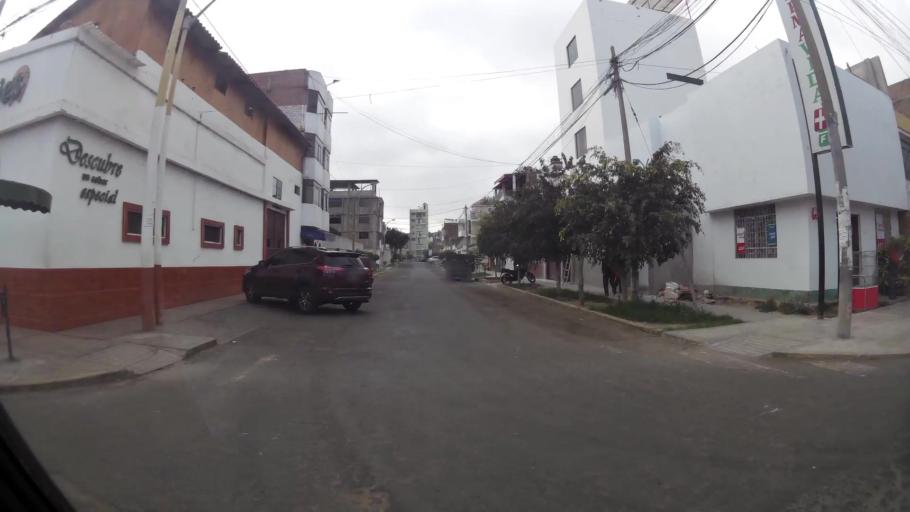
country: PE
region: La Libertad
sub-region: Provincia de Trujillo
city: Trujillo
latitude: -8.0994
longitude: -79.0253
